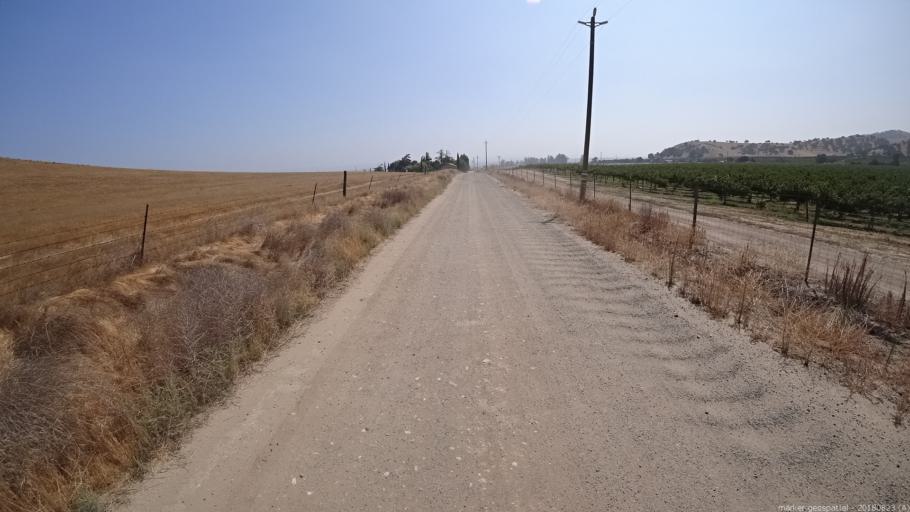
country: US
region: California
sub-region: Monterey County
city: King City
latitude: 36.2273
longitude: -121.1883
